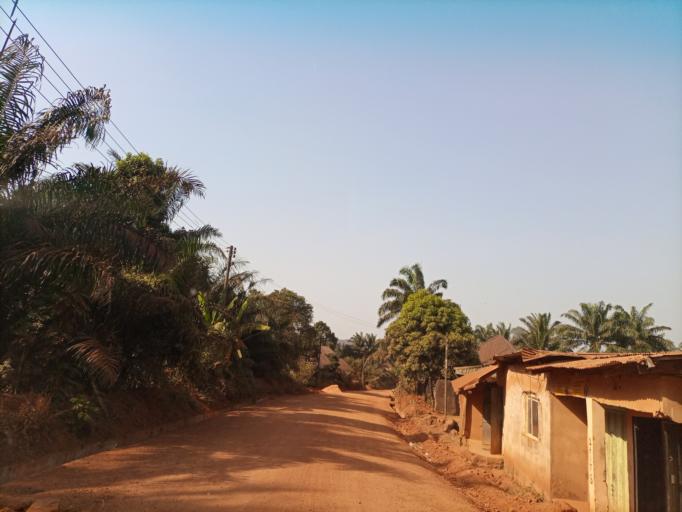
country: NG
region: Enugu
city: Aku
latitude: 6.6953
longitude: 7.3265
